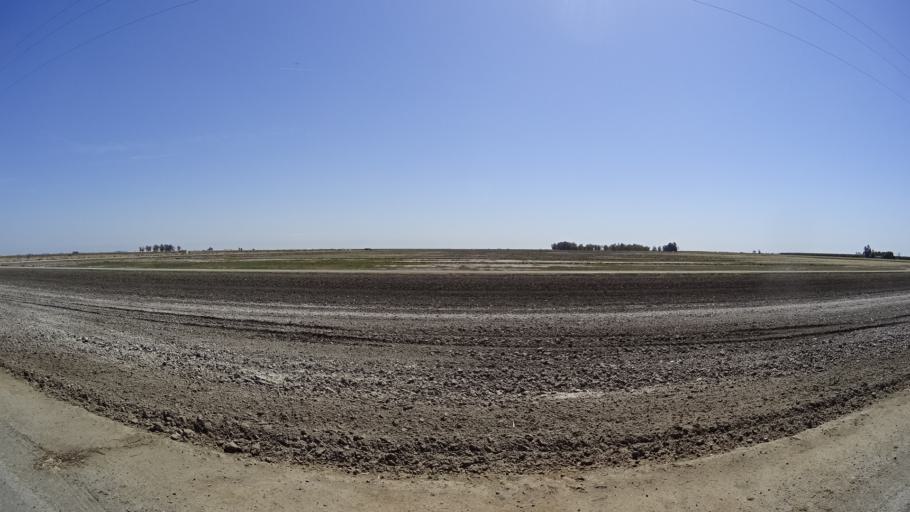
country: US
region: California
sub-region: Kings County
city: Stratford
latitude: 36.1735
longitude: -119.7802
